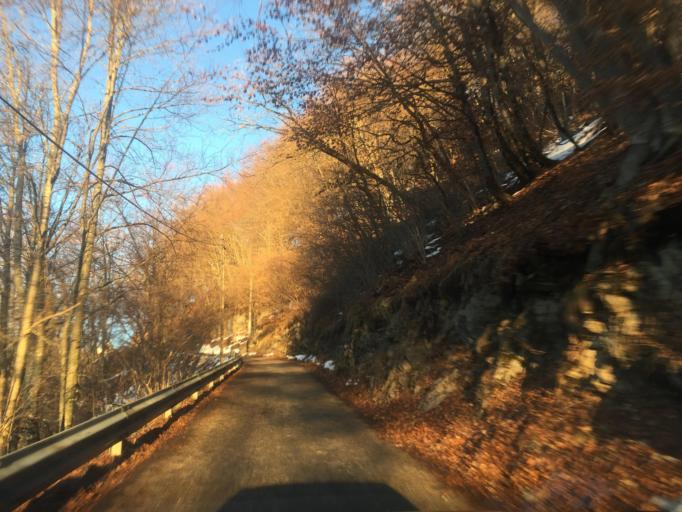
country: IT
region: Friuli Venezia Giulia
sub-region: Provincia di Udine
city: Lauco
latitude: 46.4446
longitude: 12.9360
